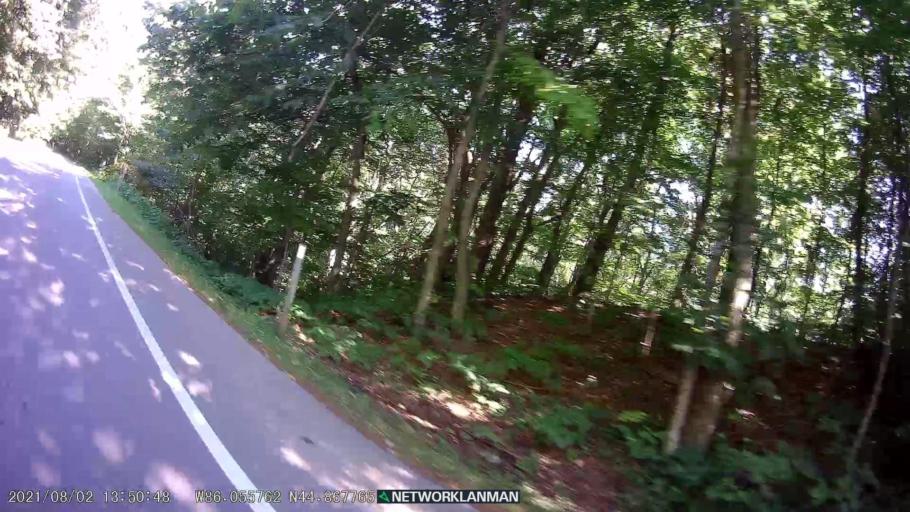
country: US
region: Michigan
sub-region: Benzie County
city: Beulah
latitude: 44.8678
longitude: -86.0556
